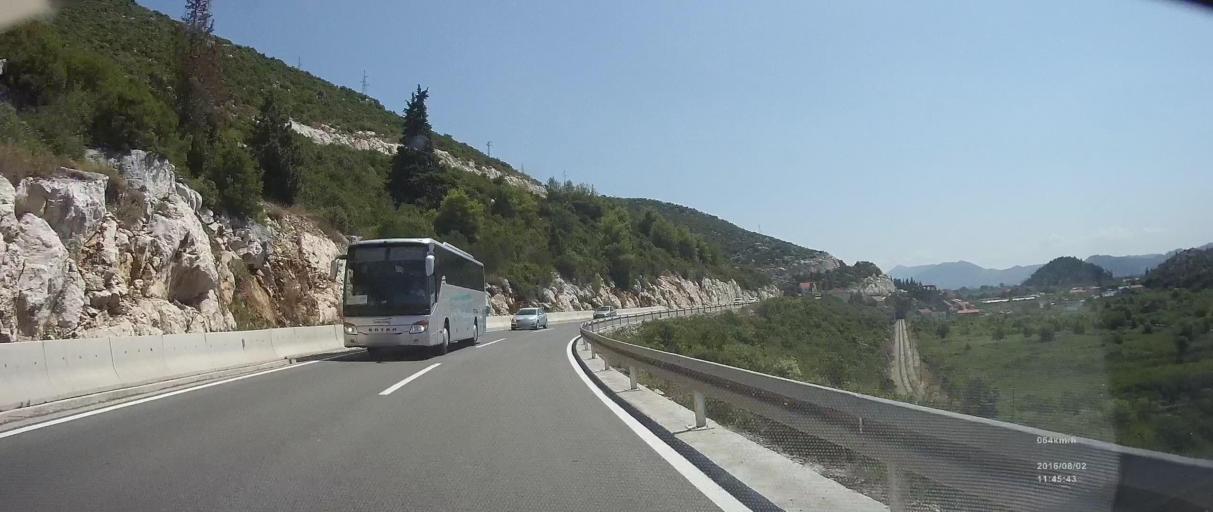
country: HR
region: Dubrovacko-Neretvanska
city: Komin
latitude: 43.0542
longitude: 17.4682
